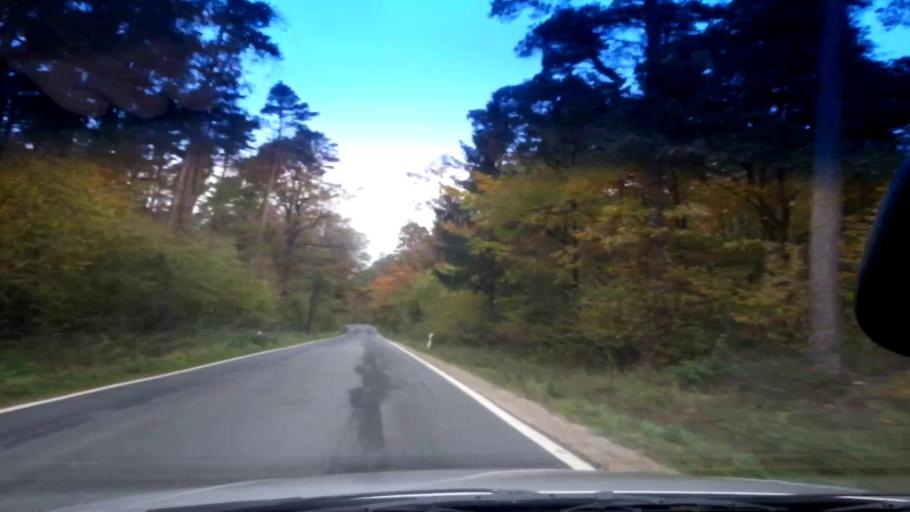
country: DE
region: Bavaria
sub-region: Upper Franconia
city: Burgebrach
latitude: 49.8116
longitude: 10.7849
